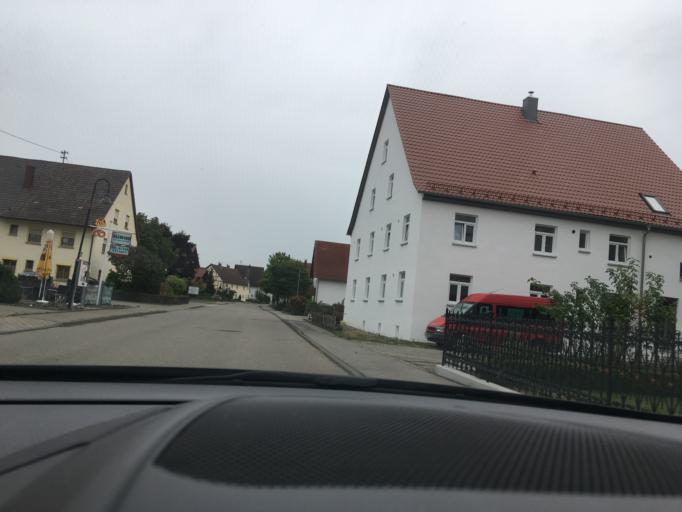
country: DE
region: Baden-Wuerttemberg
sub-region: Tuebingen Region
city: Kirchdorf
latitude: 48.0771
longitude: 10.1261
